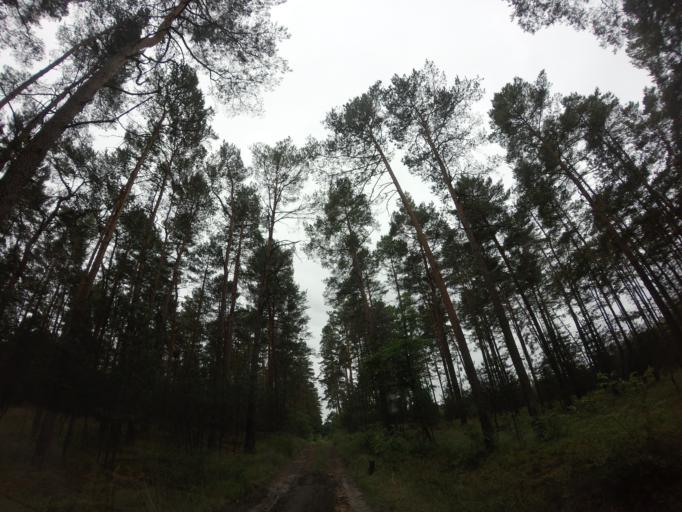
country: PL
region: West Pomeranian Voivodeship
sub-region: Powiat choszczenski
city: Drawno
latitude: 53.1364
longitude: 15.7724
